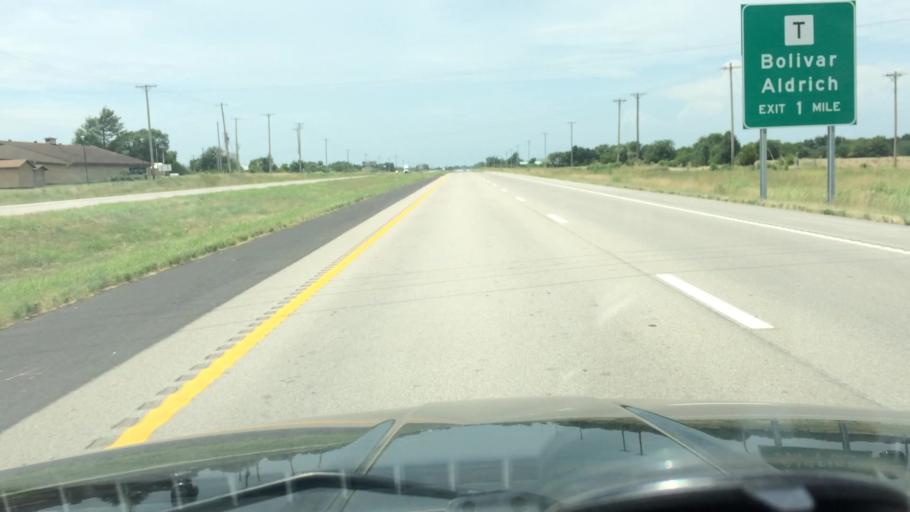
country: US
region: Missouri
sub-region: Polk County
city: Bolivar
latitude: 37.5822
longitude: -93.4105
